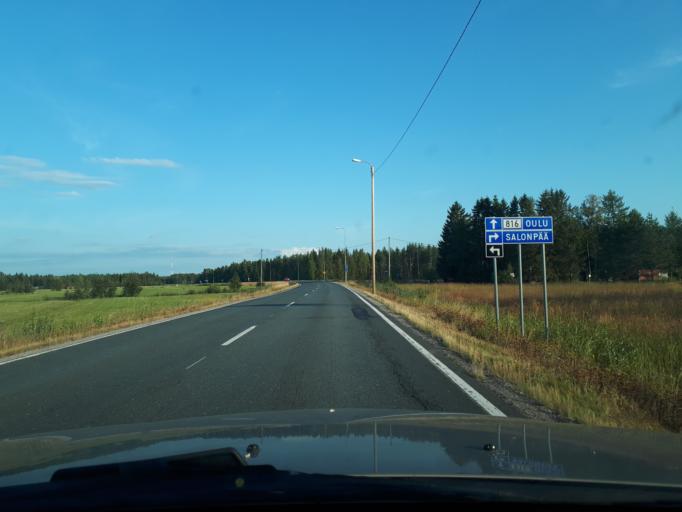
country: FI
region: Northern Ostrobothnia
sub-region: Oulu
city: Oulunsalo
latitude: 64.9815
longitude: 25.2718
